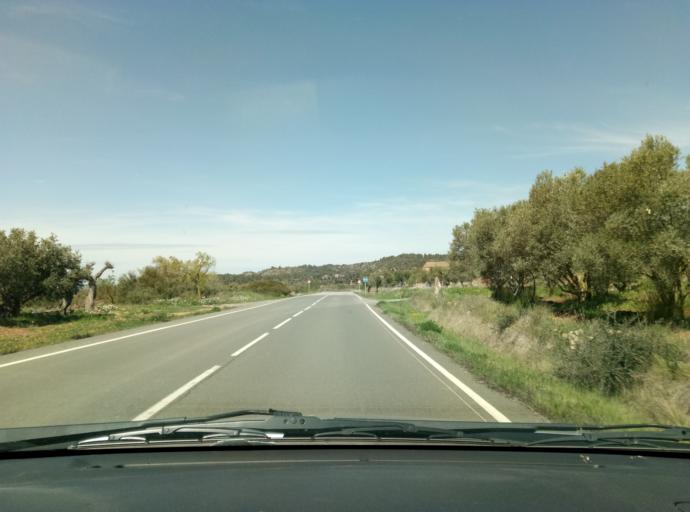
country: ES
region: Catalonia
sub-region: Provincia de Lleida
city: Vinaixa
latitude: 41.4255
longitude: 0.8920
